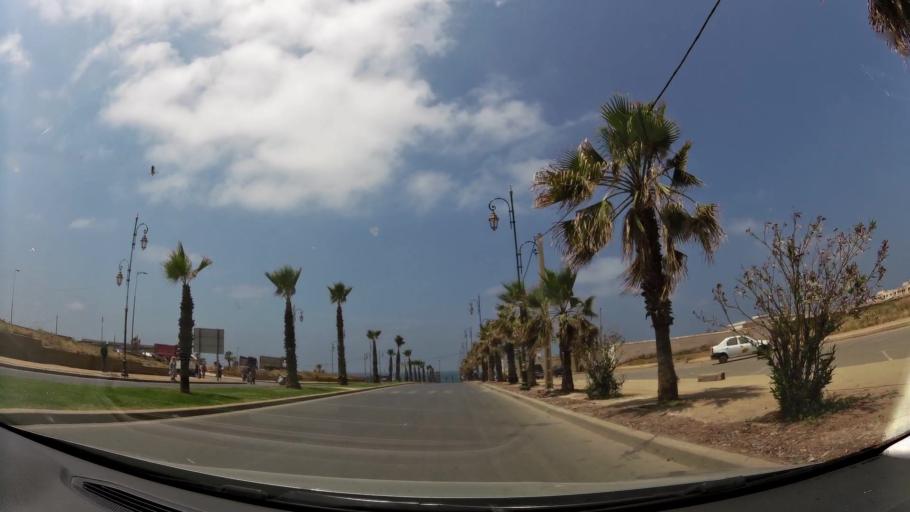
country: MA
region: Rabat-Sale-Zemmour-Zaer
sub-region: Rabat
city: Rabat
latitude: 34.0065
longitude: -6.8649
